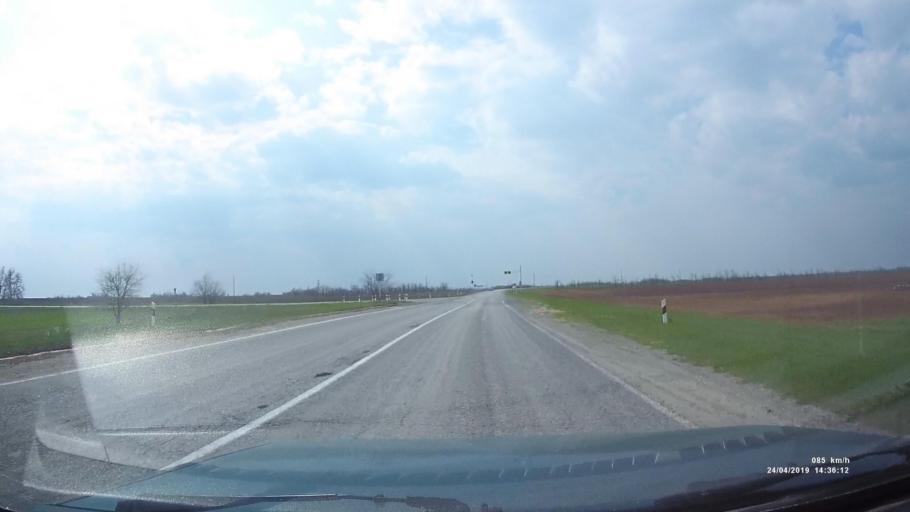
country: RU
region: Rostov
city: Remontnoye
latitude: 46.3748
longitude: 43.8954
